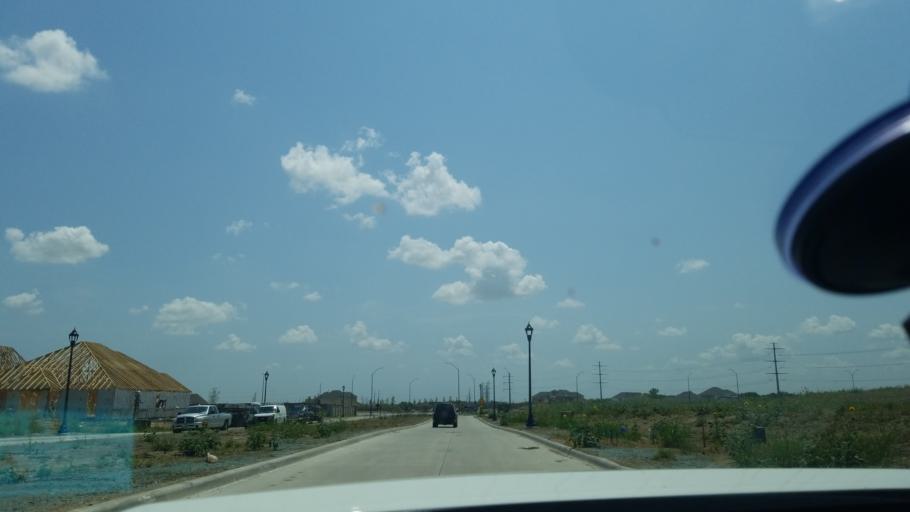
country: US
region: Texas
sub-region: Tarrant County
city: Haslet
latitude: 32.9462
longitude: -97.3981
